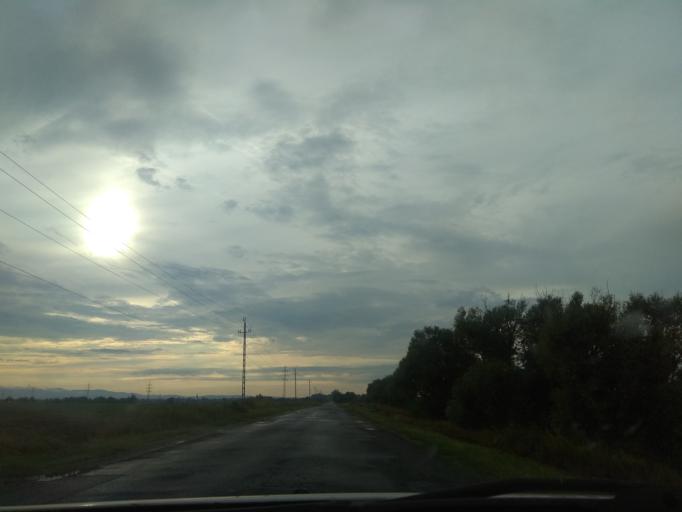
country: HU
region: Borsod-Abauj-Zemplen
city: Onga
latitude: 48.1143
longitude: 20.9427
